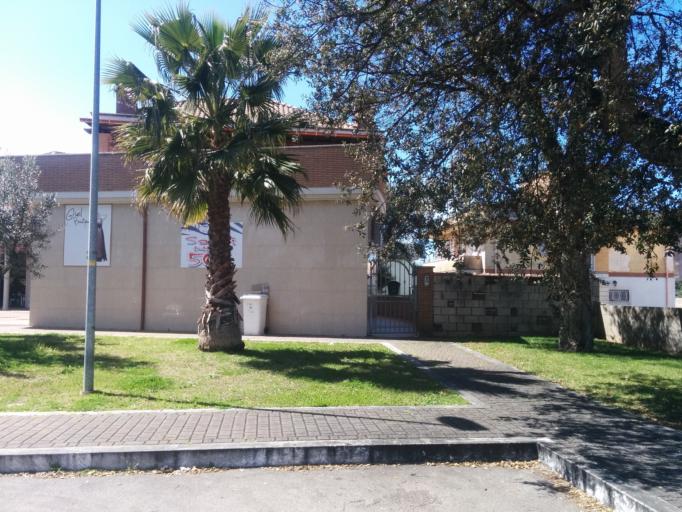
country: IT
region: Latium
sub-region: Citta metropolitana di Roma Capitale
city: Lavinio
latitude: 41.4970
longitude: 12.5909
